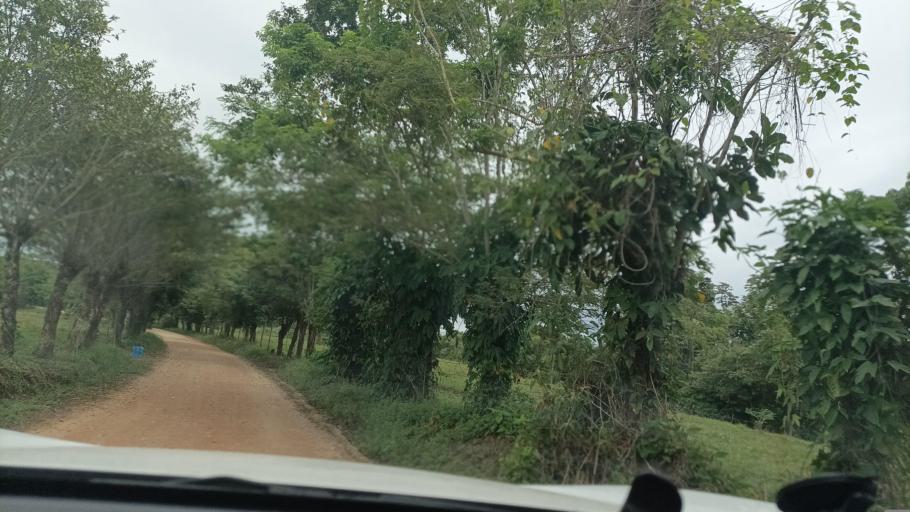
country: MX
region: Veracruz
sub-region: Uxpanapa
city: Poblado Cinco
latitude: 17.4792
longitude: -94.5699
